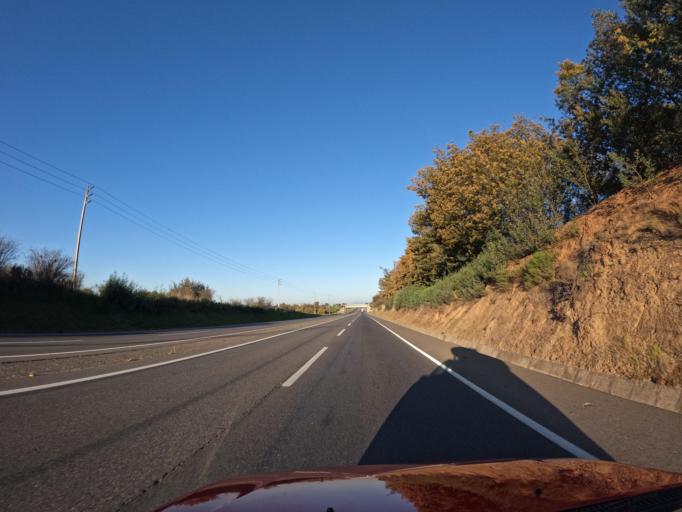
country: CL
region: Biobio
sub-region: Provincia de Nuble
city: Bulnes
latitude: -36.6588
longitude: -72.2873
